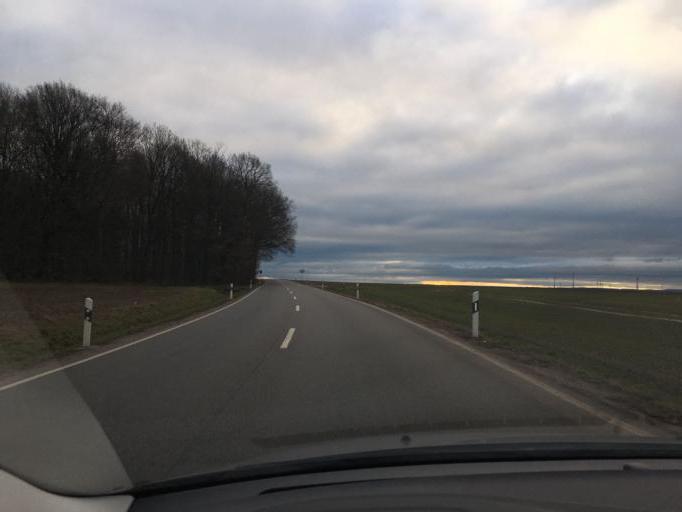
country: DE
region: Thuringia
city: Langenleuba-Niederhain
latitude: 50.9753
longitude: 12.6205
